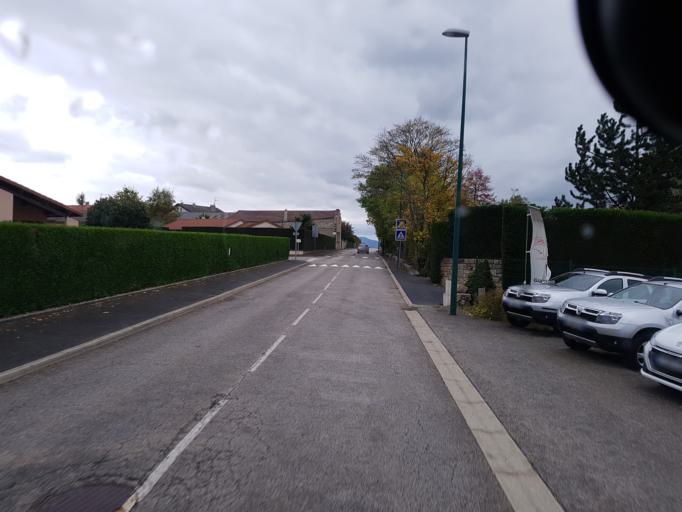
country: FR
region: Auvergne
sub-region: Departement de la Haute-Loire
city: Sainte-Sigolene
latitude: 45.2376
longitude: 4.2322
